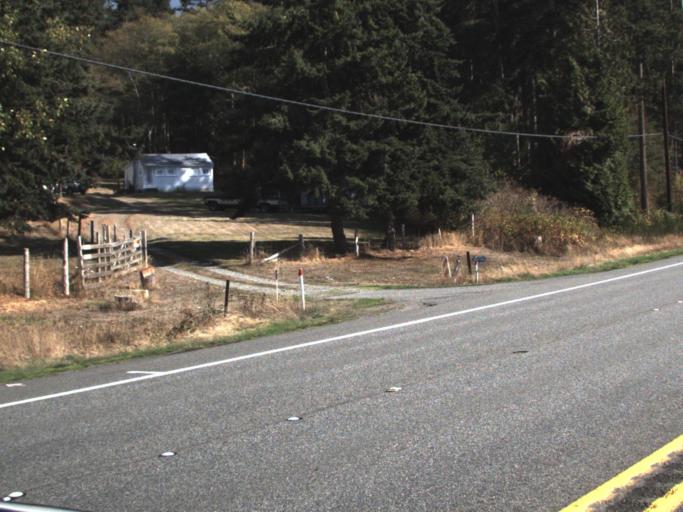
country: US
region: Washington
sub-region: Island County
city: Ault Field
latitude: 48.3625
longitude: -122.6472
